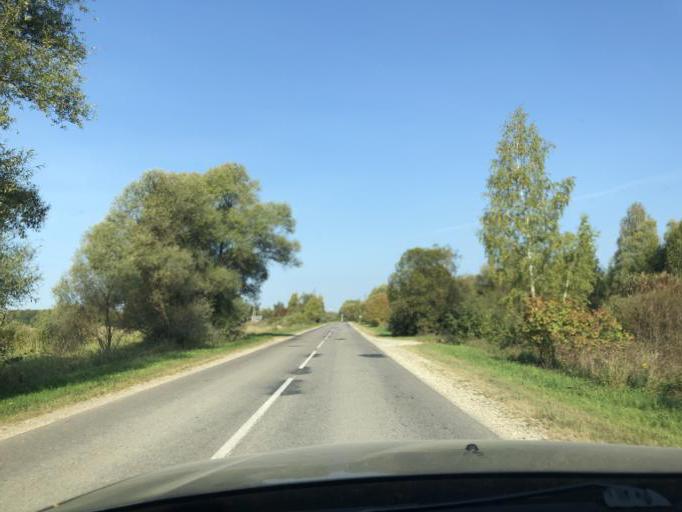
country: RU
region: Tula
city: Leninskiy
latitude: 54.3381
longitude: 37.3771
